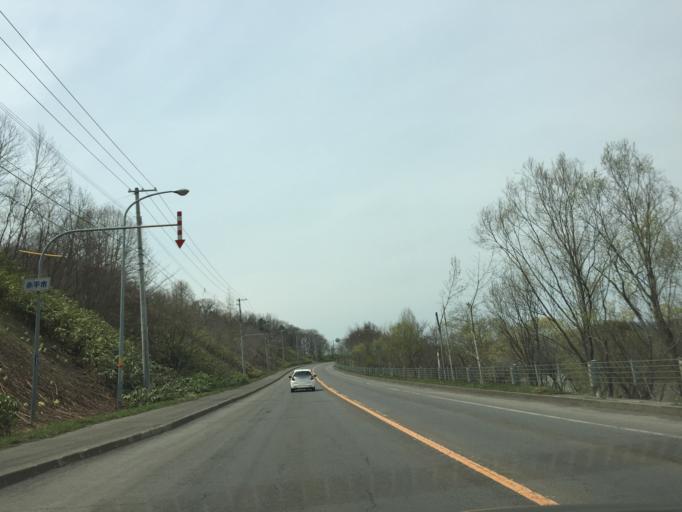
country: JP
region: Hokkaido
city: Ashibetsu
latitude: 43.5345
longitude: 142.1480
